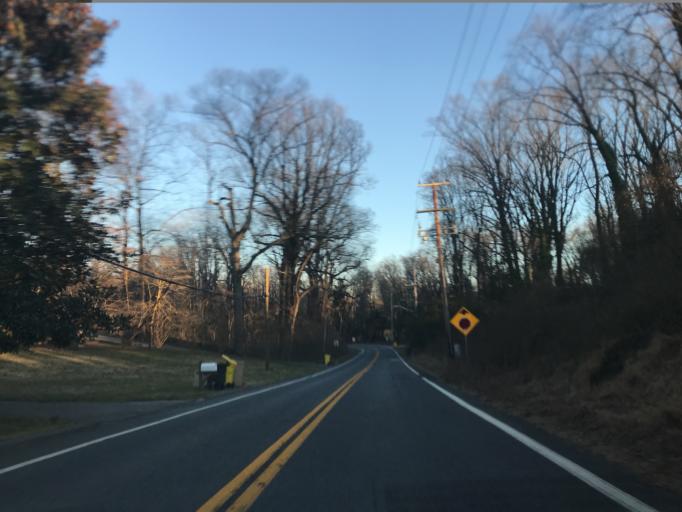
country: US
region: Maryland
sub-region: Anne Arundel County
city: Naval Academy
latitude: 39.0034
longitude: -76.4798
